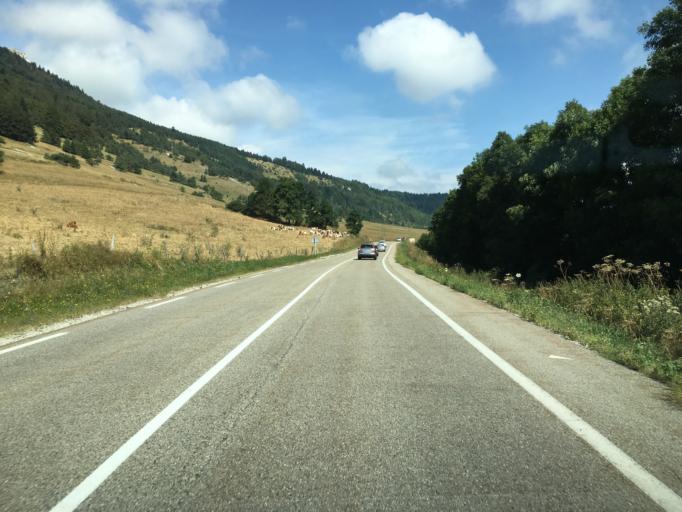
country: FR
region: Rhone-Alpes
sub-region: Departement de l'Isere
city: Mens
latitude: 44.7166
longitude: 5.6765
